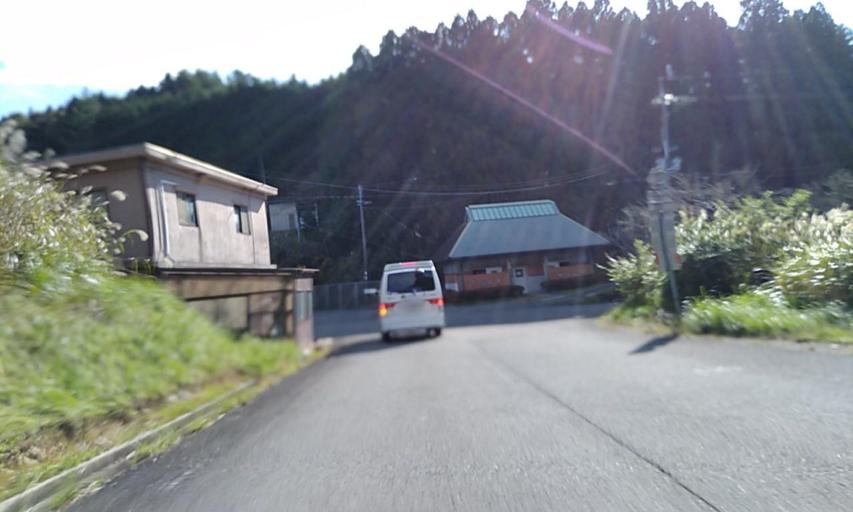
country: JP
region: Wakayama
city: Iwade
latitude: 34.1163
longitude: 135.3462
